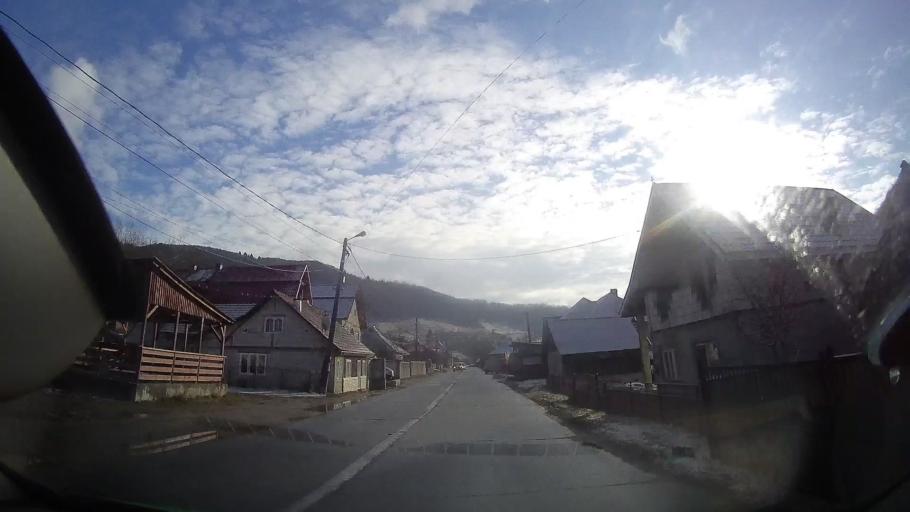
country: RO
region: Alba
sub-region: Comuna Sohodol
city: Sohodol
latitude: 46.3709
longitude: 23.0233
